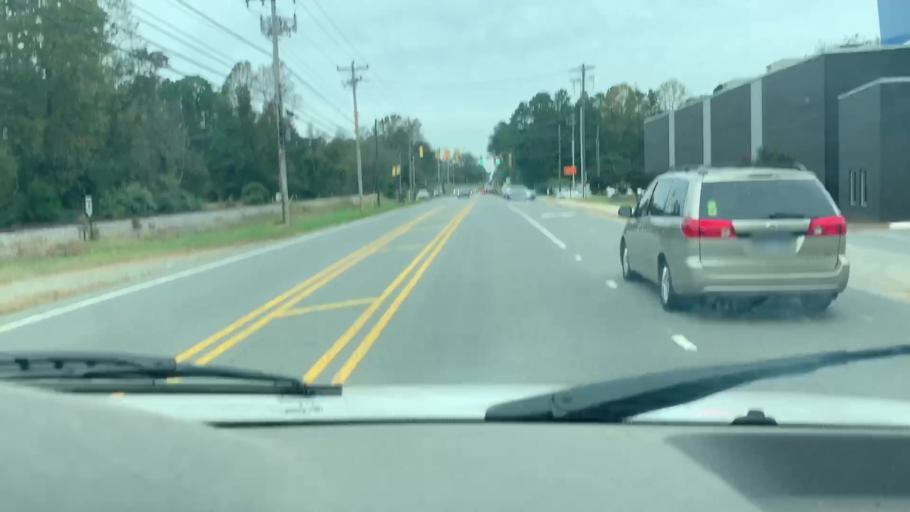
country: US
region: North Carolina
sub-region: Gaston County
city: Davidson
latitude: 35.5345
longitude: -80.8466
